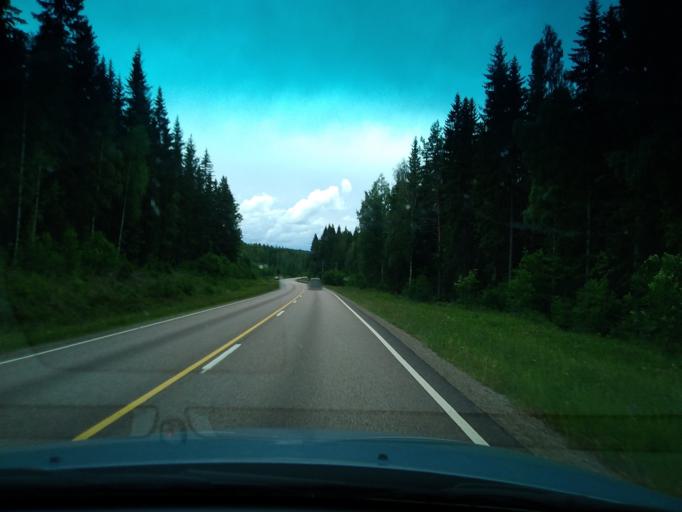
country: FI
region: Central Finland
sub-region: Keuruu
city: Multia
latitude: 62.3713
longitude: 24.7408
